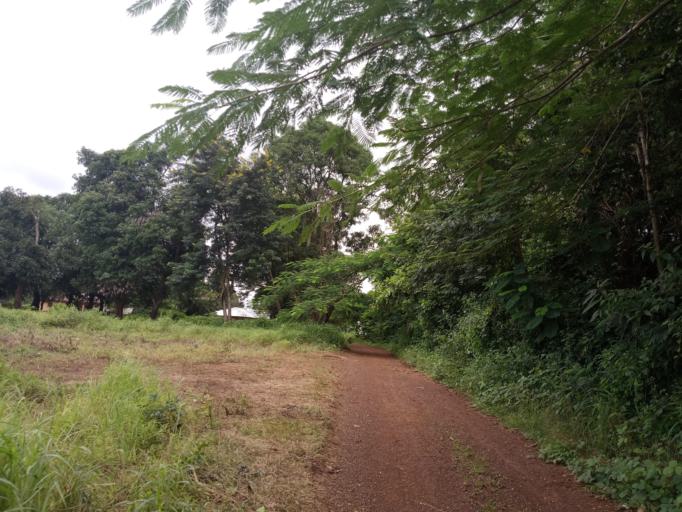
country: SL
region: Northern Province
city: Kamakwie
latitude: 9.4810
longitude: -12.2437
